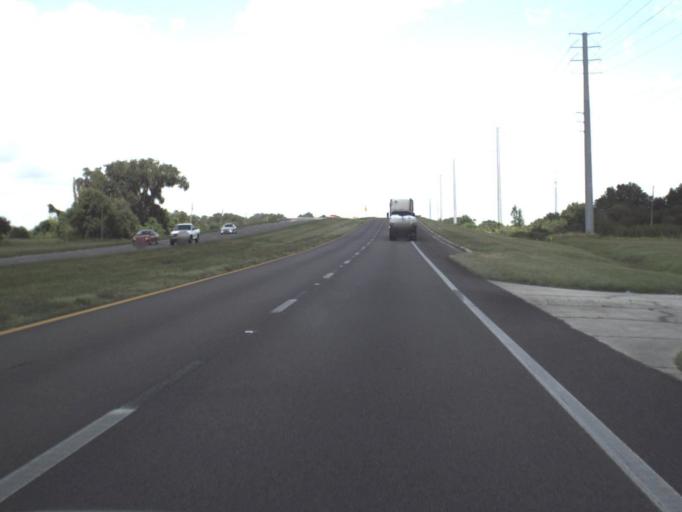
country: US
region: Florida
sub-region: Polk County
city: Fort Meade
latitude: 27.8123
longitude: -81.8205
